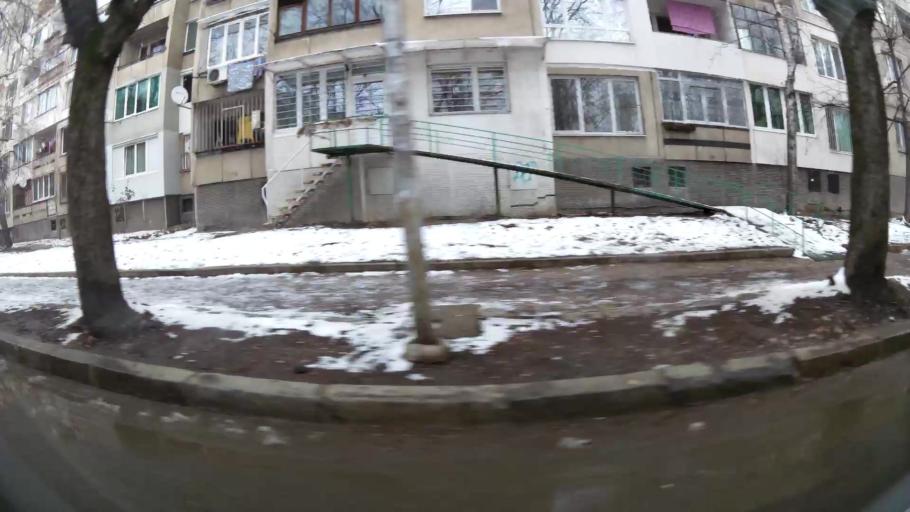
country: BG
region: Sofia-Capital
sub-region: Stolichna Obshtina
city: Sofia
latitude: 42.7098
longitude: 23.2974
